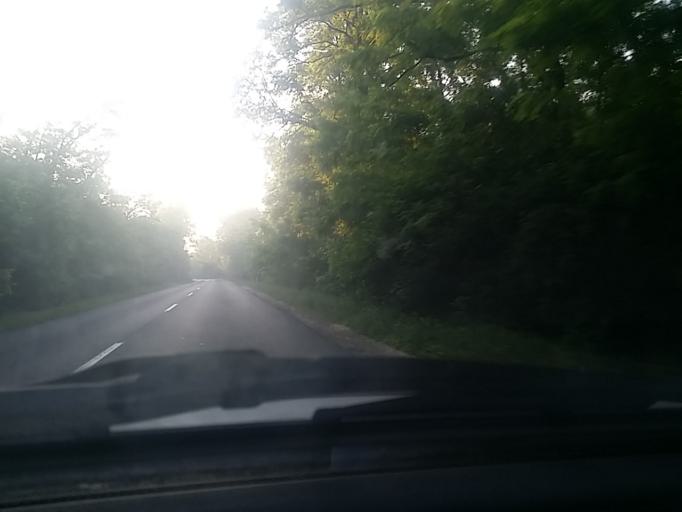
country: HU
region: Pest
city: Forropuszta
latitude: 47.4636
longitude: 19.6430
